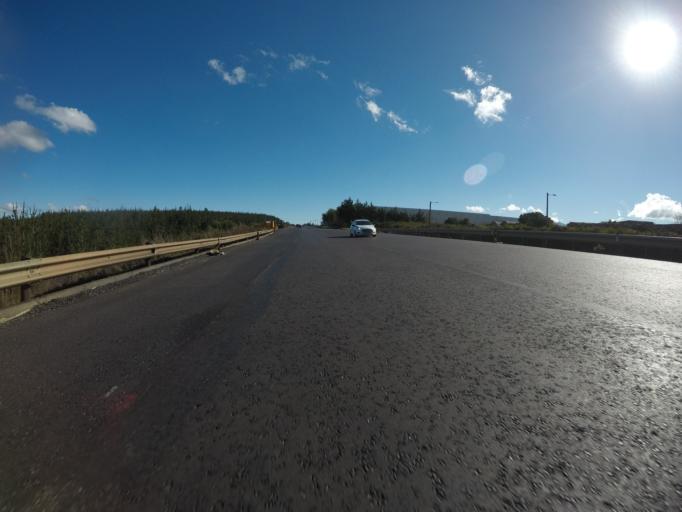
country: ZA
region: Western Cape
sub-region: Overberg District Municipality
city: Grabouw
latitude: -34.1784
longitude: 19.0746
